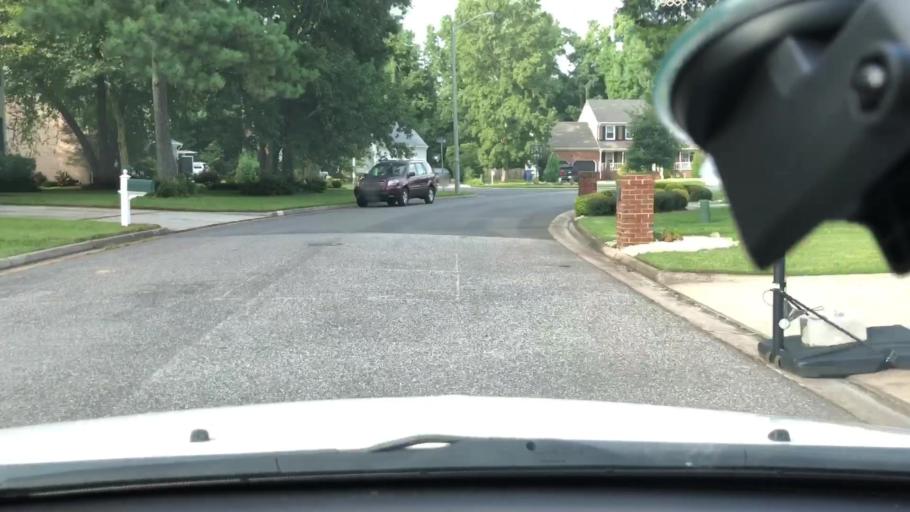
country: US
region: Virginia
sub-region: City of Chesapeake
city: Chesapeake
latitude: 36.7175
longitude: -76.2745
